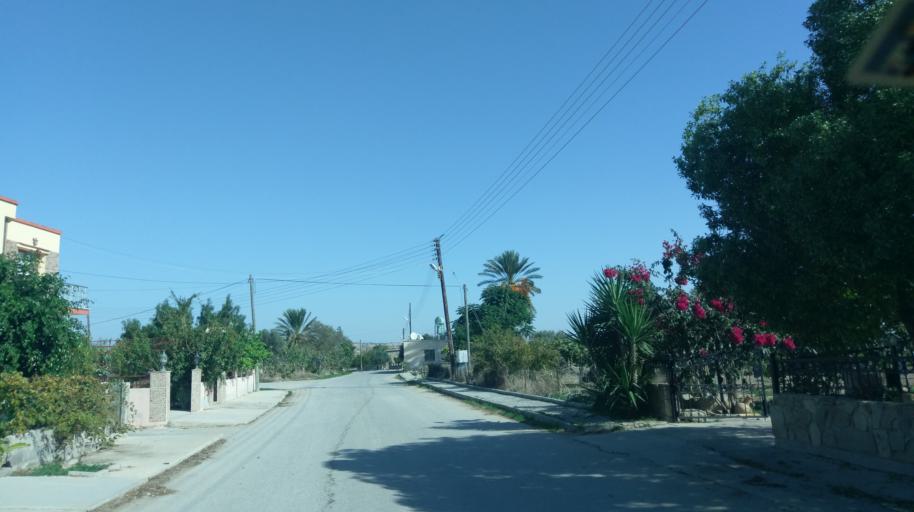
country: CY
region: Ammochostos
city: Leonarisso
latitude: 35.3894
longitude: 34.0148
